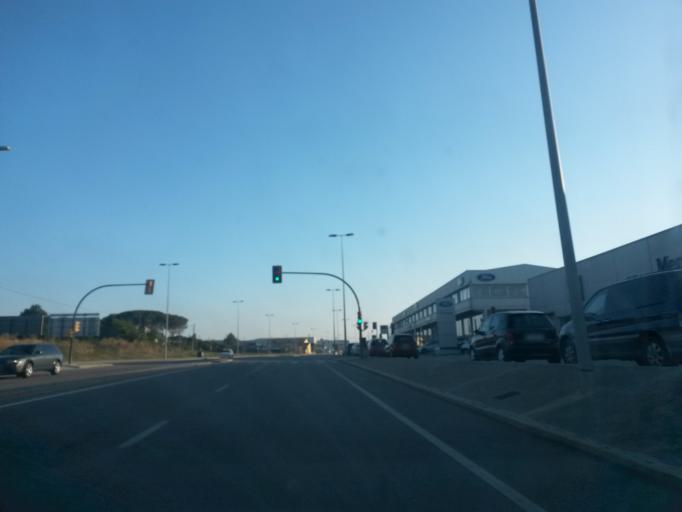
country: ES
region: Catalonia
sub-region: Provincia de Girona
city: Fornells de la Selva
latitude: 41.9391
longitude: 2.8017
